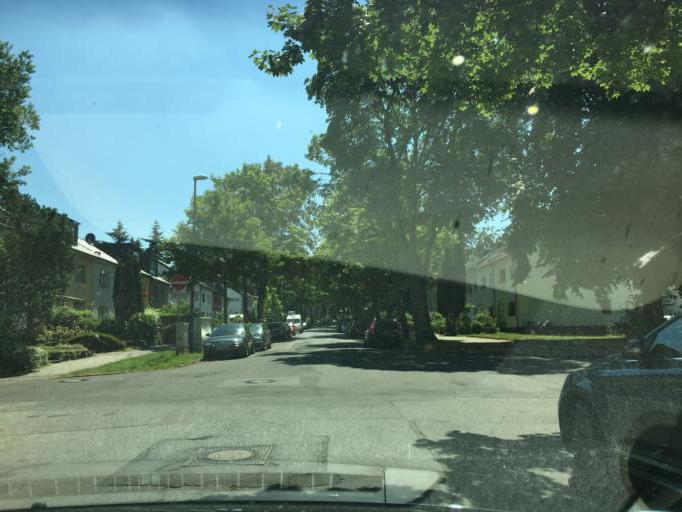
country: DE
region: North Rhine-Westphalia
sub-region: Regierungsbezirk Koln
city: Aachen
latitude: 50.7547
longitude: 6.0913
